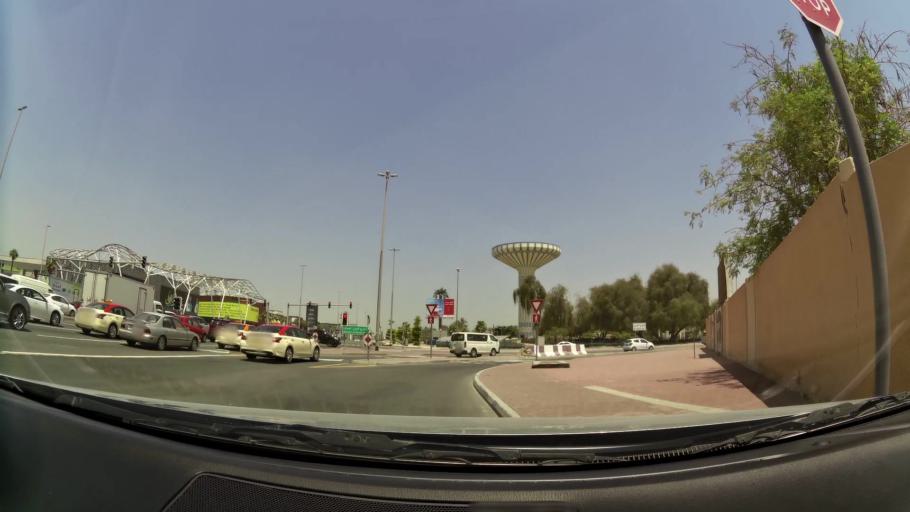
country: AE
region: Dubai
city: Dubai
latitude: 25.2078
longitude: 55.2659
